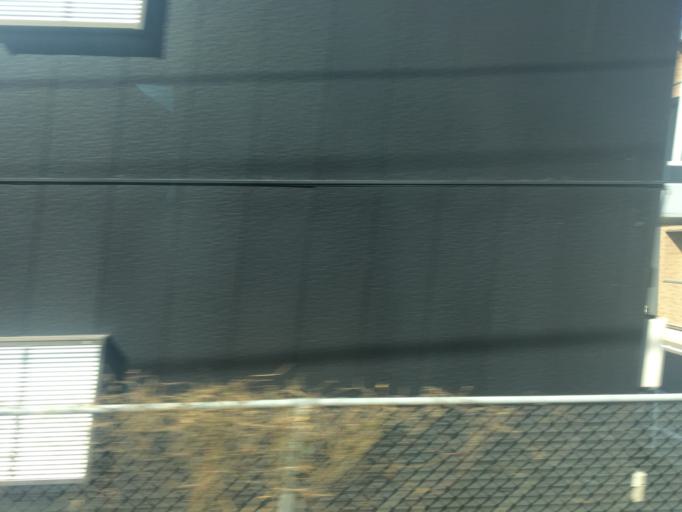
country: JP
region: Tochigi
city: Utsunomiya-shi
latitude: 36.5000
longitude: 139.8779
